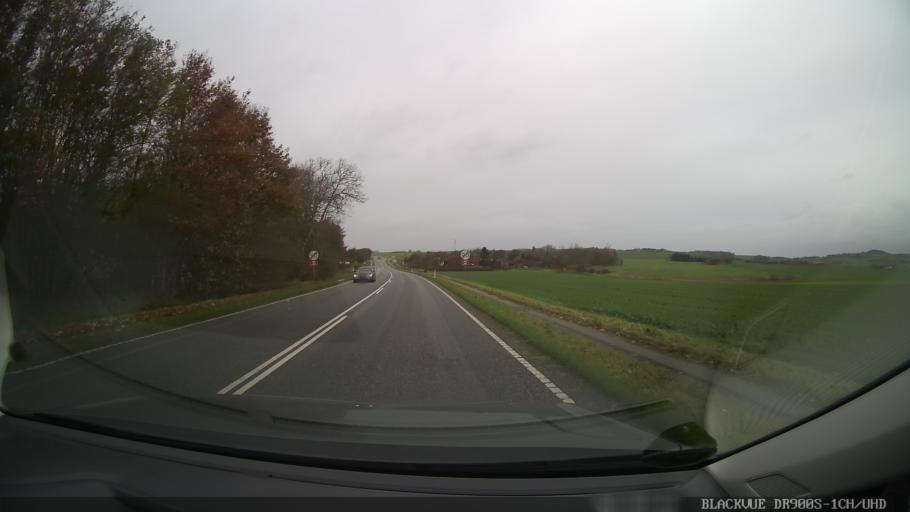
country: DK
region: North Denmark
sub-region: Thisted Kommune
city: Thisted
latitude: 56.8516
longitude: 8.7003
